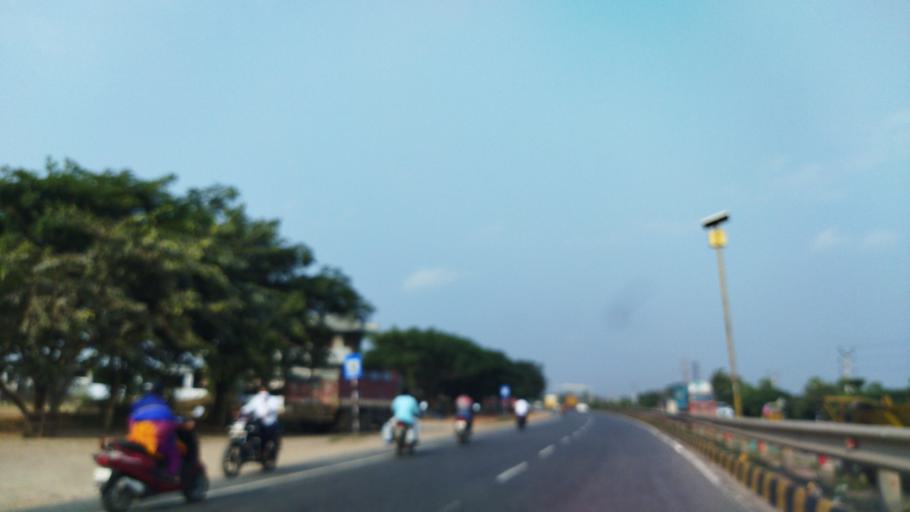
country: IN
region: Telangana
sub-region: Nalgonda
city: Nalgonda
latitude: 17.1674
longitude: 79.4056
